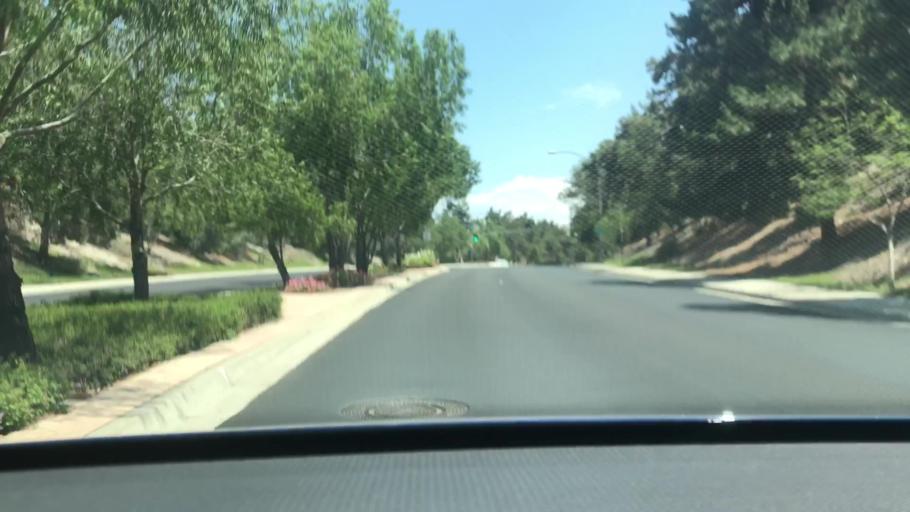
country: US
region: California
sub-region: San Diego County
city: Poway
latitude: 32.9230
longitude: -117.1013
